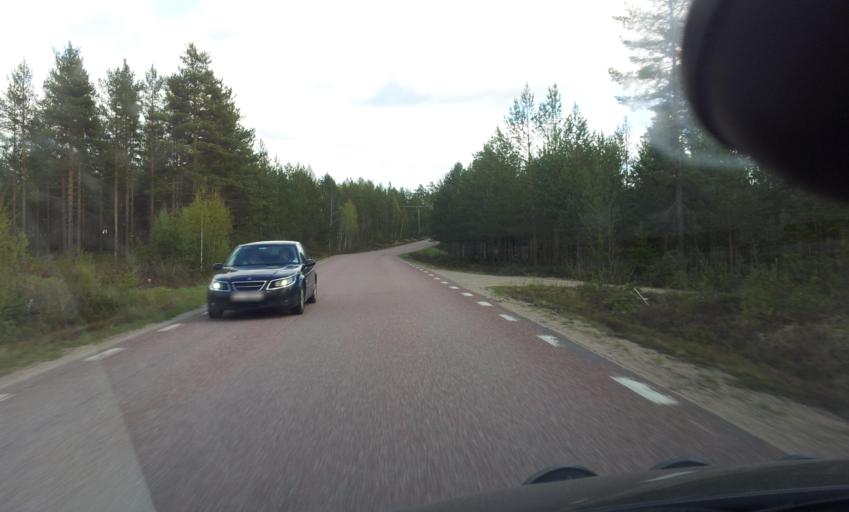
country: SE
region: Gaevleborg
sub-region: Bollnas Kommun
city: Kilafors
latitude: 61.3827
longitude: 16.6174
